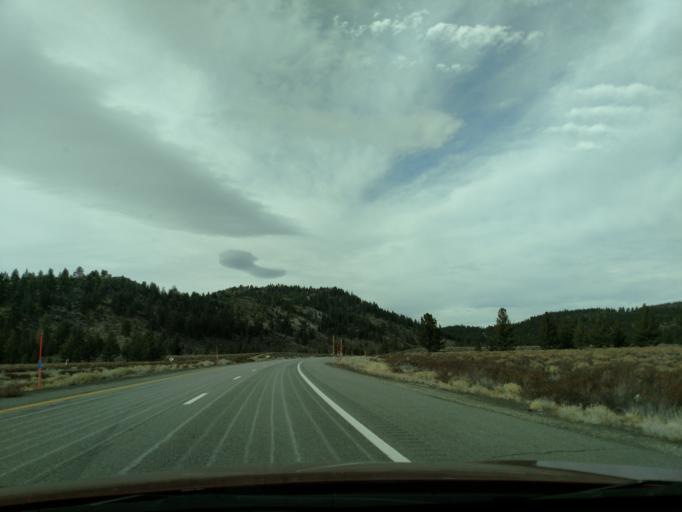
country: US
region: California
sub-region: Mono County
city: Mammoth Lakes
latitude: 37.6448
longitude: -118.9218
